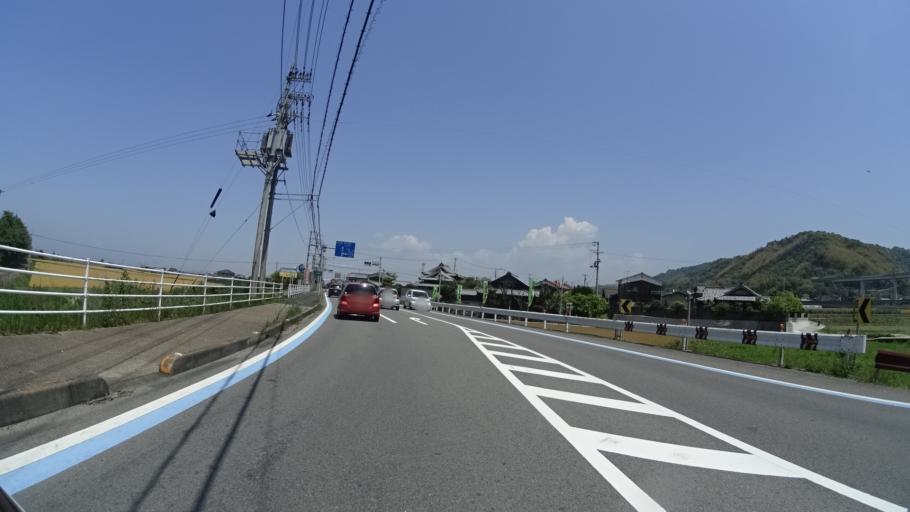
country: JP
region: Ehime
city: Iyo
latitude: 33.7334
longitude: 132.6912
